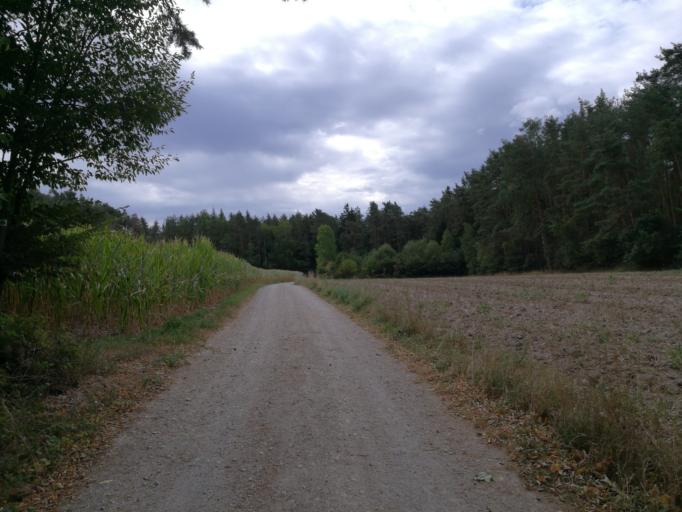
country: DE
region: Bavaria
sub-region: Regierungsbezirk Mittelfranken
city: Seukendorf
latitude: 49.4757
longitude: 10.8947
